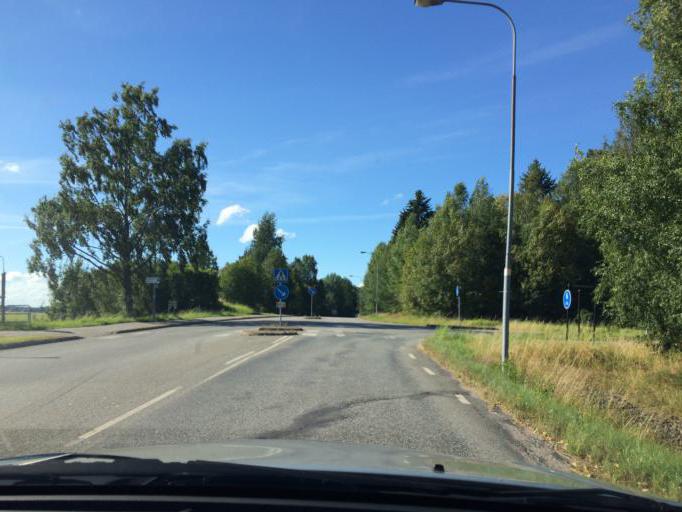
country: SE
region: Vaestmanland
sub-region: Vasteras
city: Vasteras
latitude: 59.6014
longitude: 16.6263
